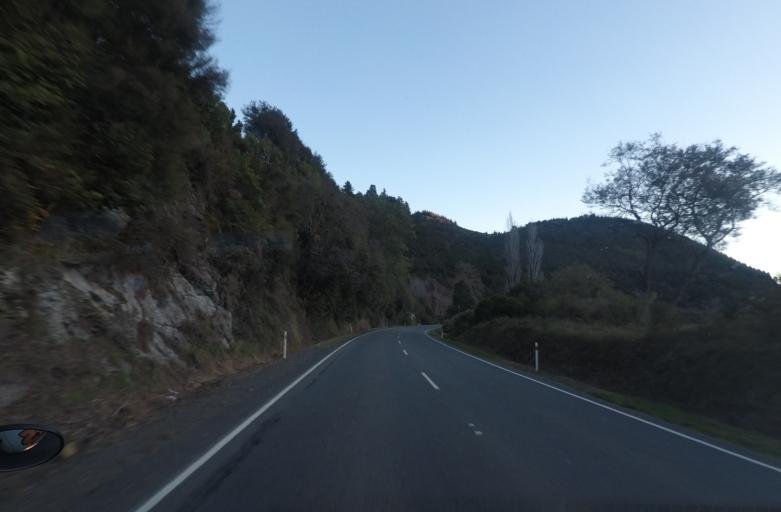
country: NZ
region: Marlborough
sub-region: Marlborough District
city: Picton
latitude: -41.2738
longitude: 173.7443
